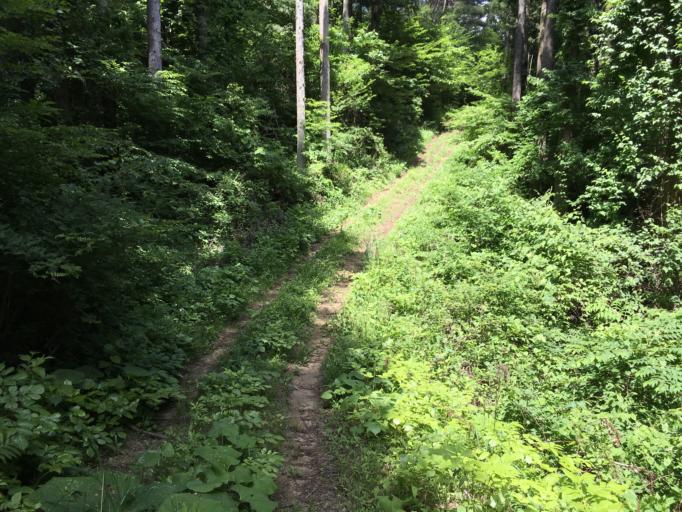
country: JP
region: Miyagi
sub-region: Oshika Gun
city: Onagawa Cho
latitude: 38.6902
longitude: 141.3579
